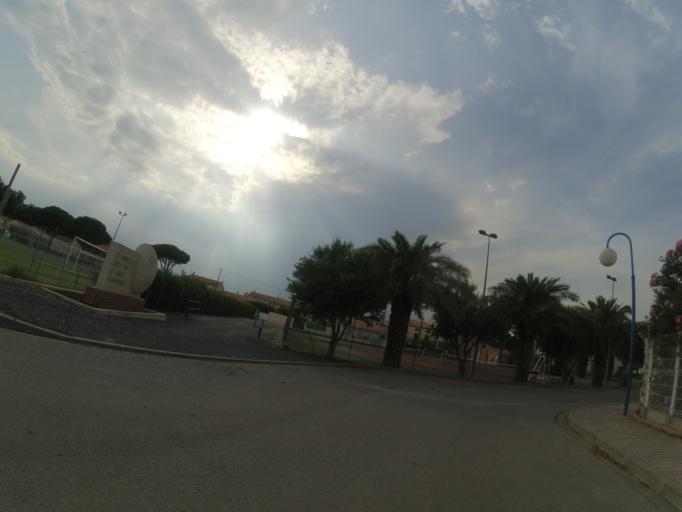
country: FR
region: Languedoc-Roussillon
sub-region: Departement des Pyrenees-Orientales
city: Corneilla-la-Riviere
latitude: 42.6817
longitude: 2.7345
